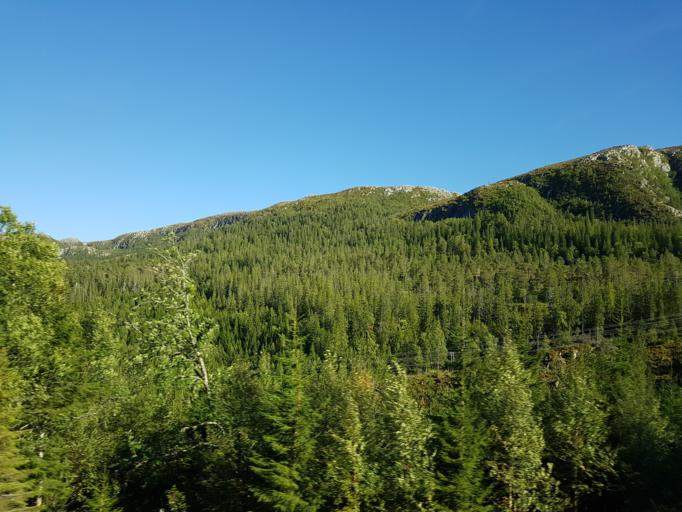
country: NO
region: Sor-Trondelag
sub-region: Afjord
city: A i Afjord
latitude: 63.7196
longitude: 10.2323
